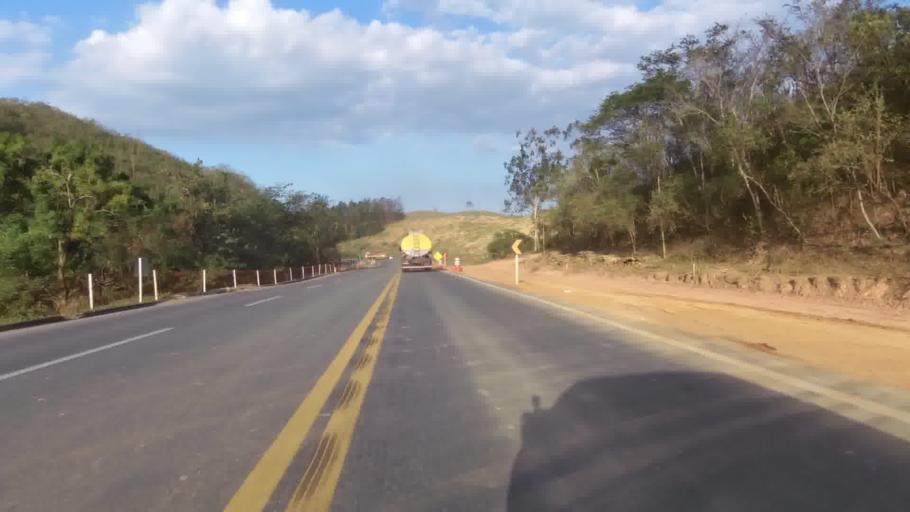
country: BR
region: Espirito Santo
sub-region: Rio Novo Do Sul
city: Rio Novo do Sul
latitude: -20.9005
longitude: -41.0168
